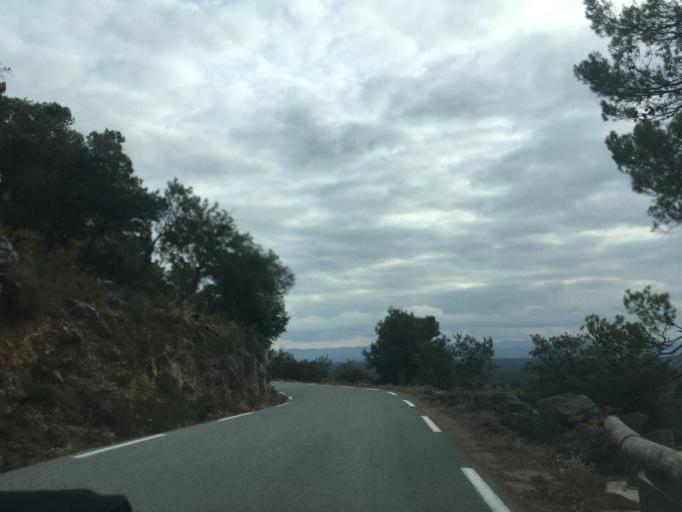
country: FR
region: Provence-Alpes-Cote d'Azur
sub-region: Departement du Var
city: Villecroze
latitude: 43.5816
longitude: 6.3102
